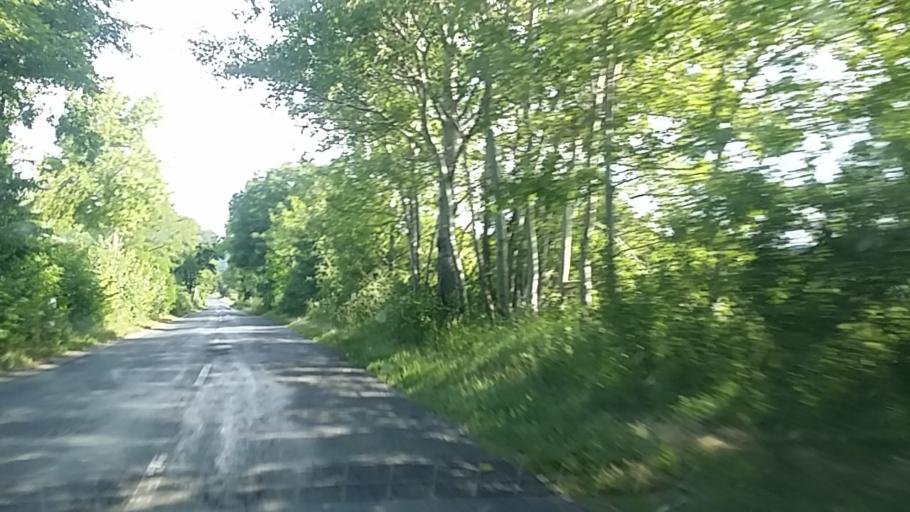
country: HU
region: Komarom-Esztergom
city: Bajna
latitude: 47.6770
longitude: 18.5731
